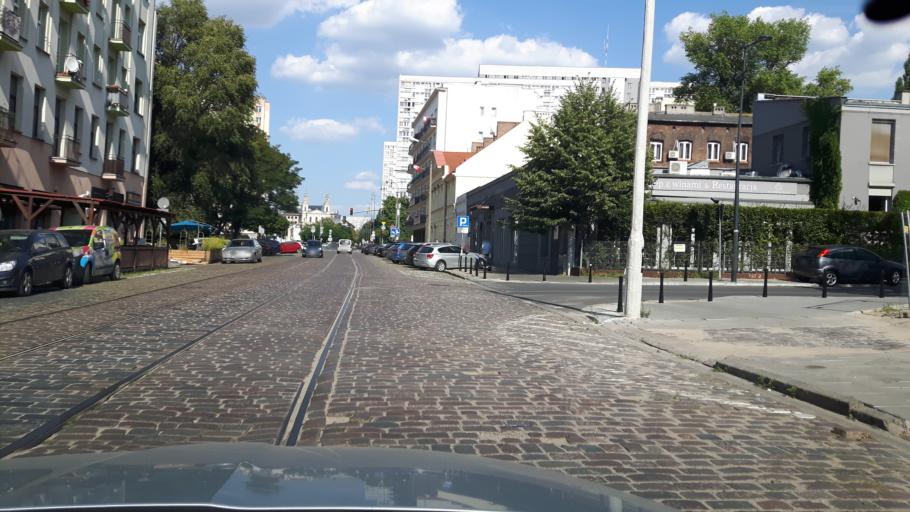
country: PL
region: Masovian Voivodeship
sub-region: Warszawa
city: Wola
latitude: 52.2368
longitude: 20.9873
